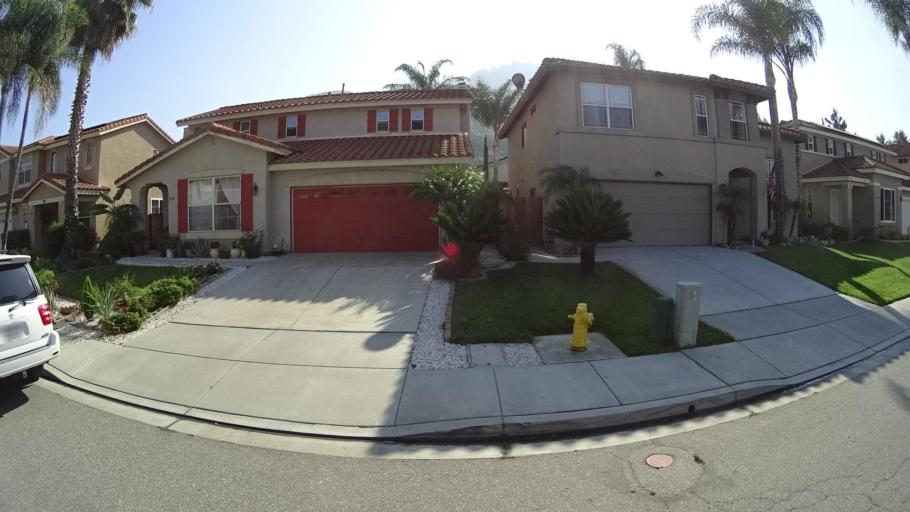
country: US
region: California
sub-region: San Diego County
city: Bonsall
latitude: 33.3240
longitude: -117.1502
